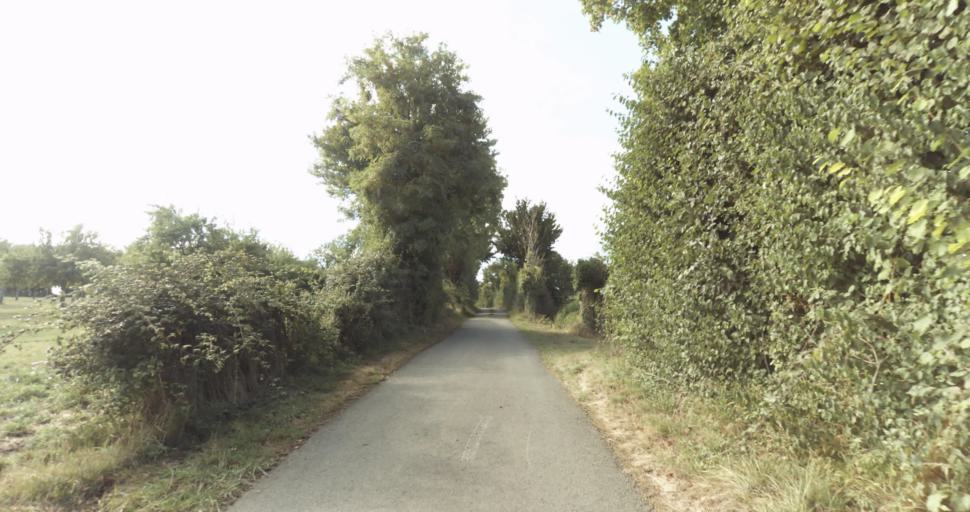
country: FR
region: Lower Normandy
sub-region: Departement de l'Orne
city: Vimoutiers
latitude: 48.9153
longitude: 0.1235
